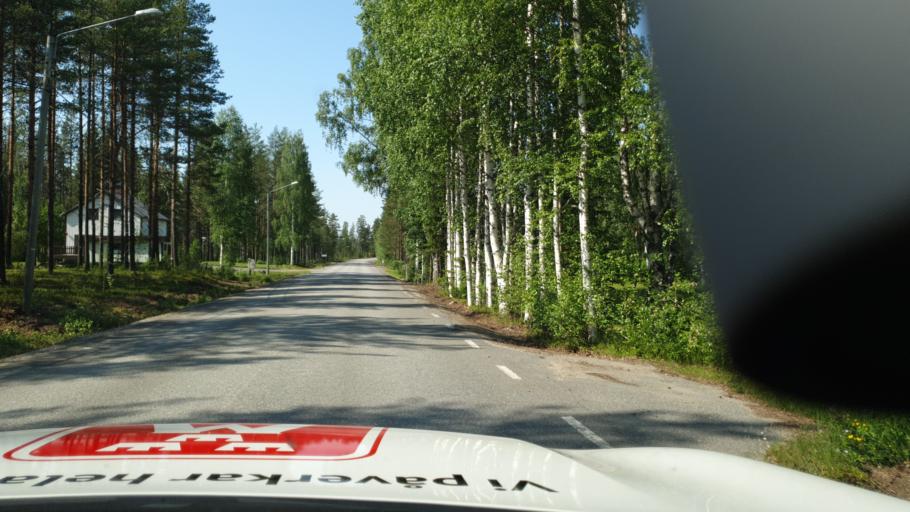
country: SE
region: Vaesterbotten
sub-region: Skelleftea Kommun
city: Langsele
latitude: 64.9395
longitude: 20.0172
